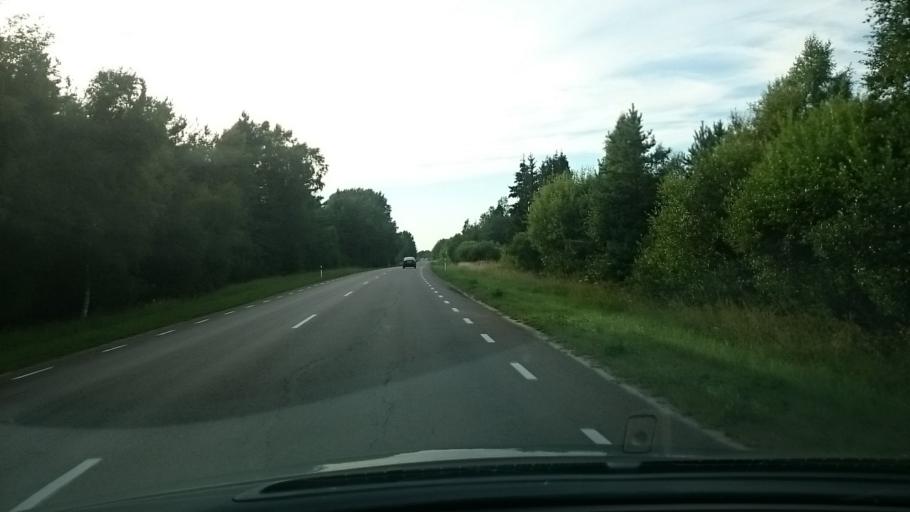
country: EE
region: Saare
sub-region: Kuressaare linn
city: Kuressaare
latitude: 58.2787
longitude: 22.4360
